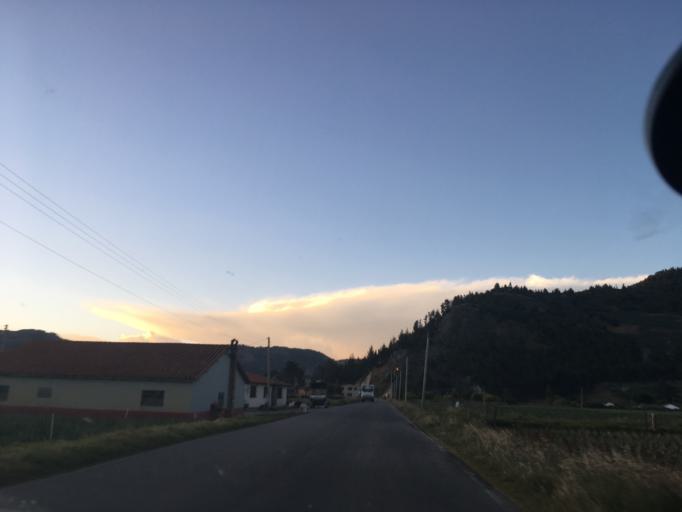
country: CO
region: Boyaca
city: Aquitania
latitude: 5.5837
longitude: -72.8966
